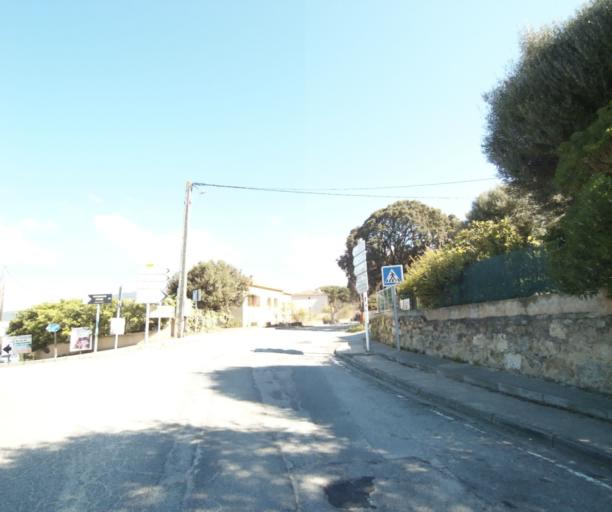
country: FR
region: Corsica
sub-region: Departement de la Corse-du-Sud
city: Propriano
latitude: 41.6718
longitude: 8.9187
